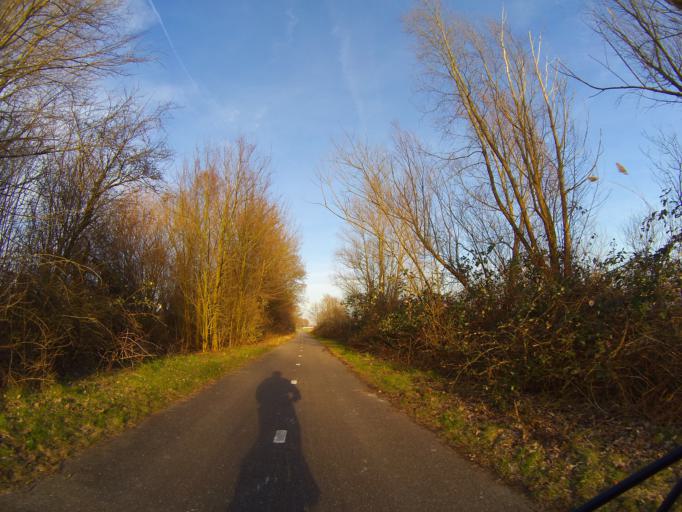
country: NL
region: Gelderland
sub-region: Gemeente Nijkerk
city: Nijkerk
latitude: 52.2616
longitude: 5.4597
